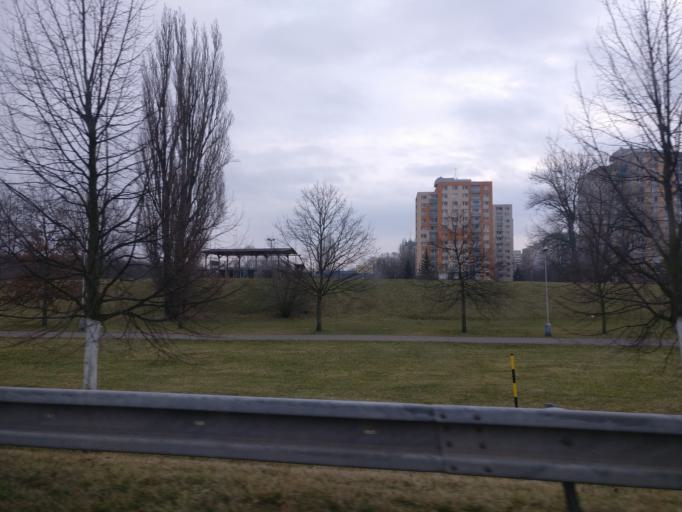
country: CZ
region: Pardubicky
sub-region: Okres Pardubice
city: Pardubice
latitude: 50.0380
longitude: 15.7534
